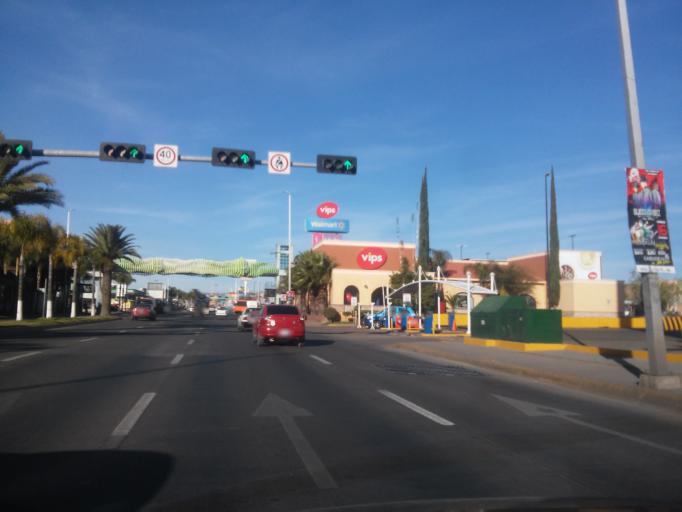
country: MX
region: Durango
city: Victoria de Durango
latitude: 24.0347
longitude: -104.6518
